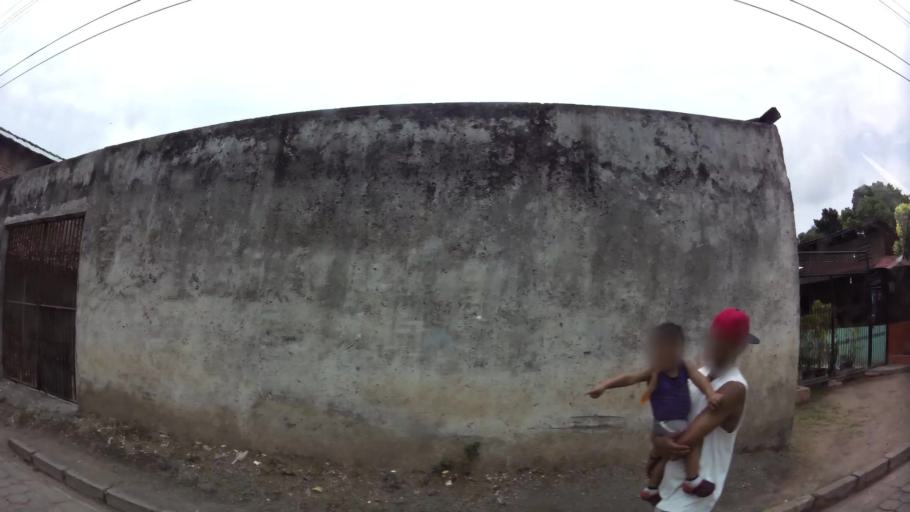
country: NI
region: Granada
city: Granada
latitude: 11.9265
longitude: -85.9632
